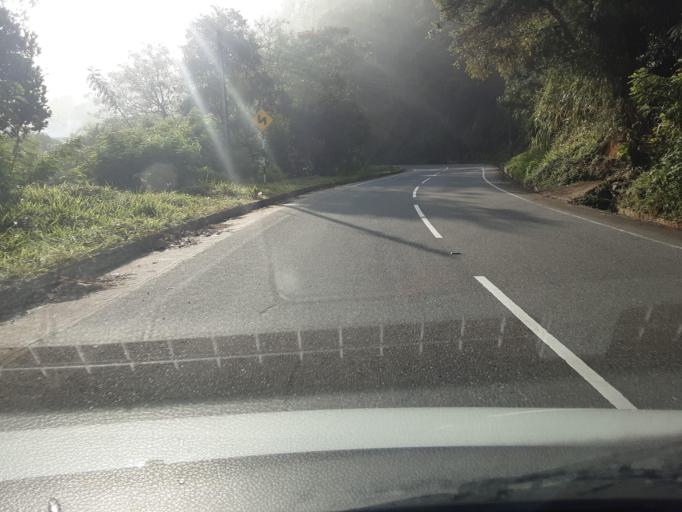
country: LK
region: Uva
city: Badulla
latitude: 6.9207
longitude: 80.9616
